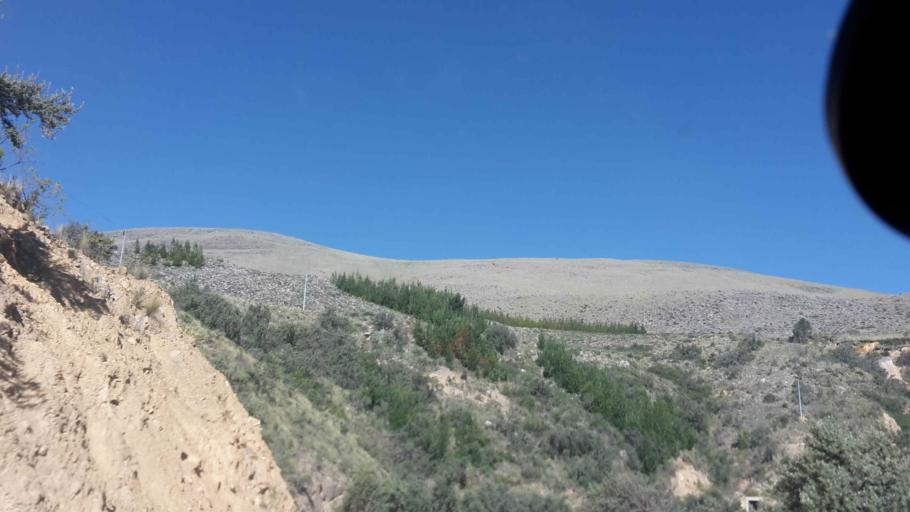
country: BO
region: Cochabamba
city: Arani
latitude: -17.6769
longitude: -65.7248
